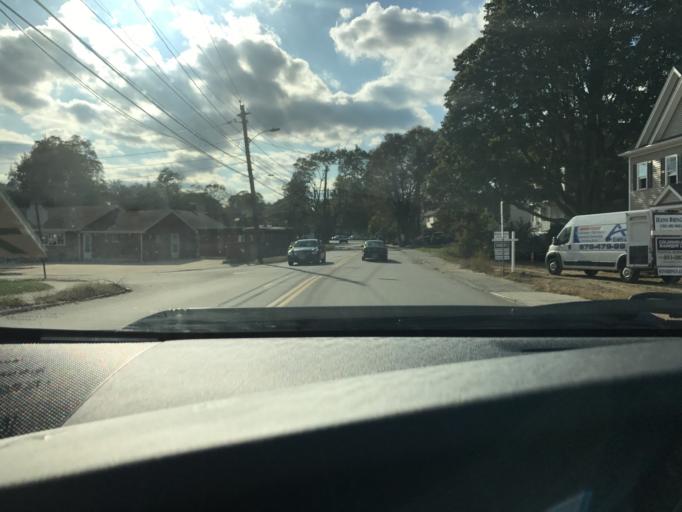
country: US
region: Massachusetts
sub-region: Middlesex County
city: Watertown
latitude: 42.3818
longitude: -71.2009
